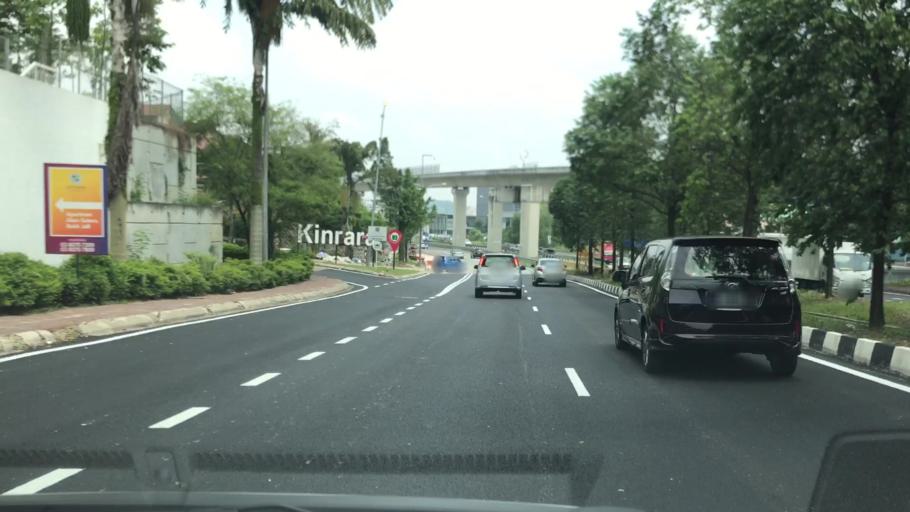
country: MY
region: Selangor
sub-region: Petaling
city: Petaling Jaya
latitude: 3.0556
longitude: 101.6600
